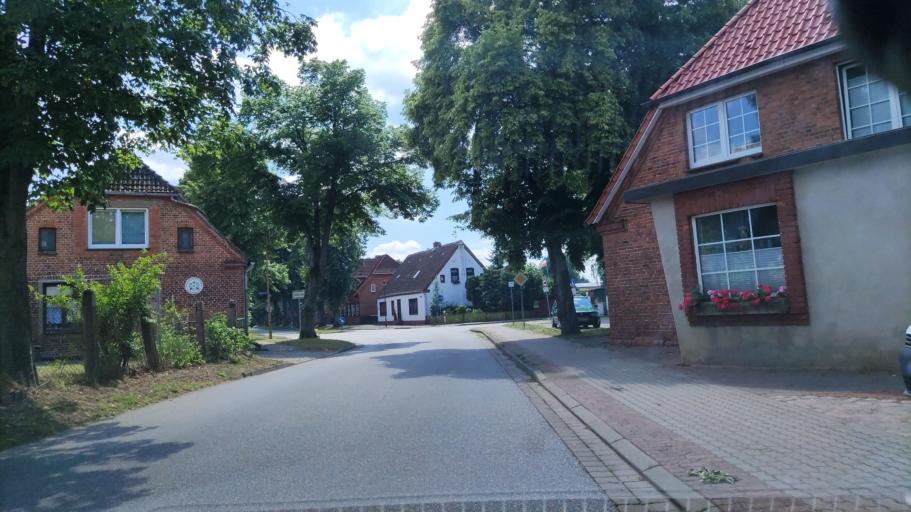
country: DE
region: Mecklenburg-Vorpommern
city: Lubtheen
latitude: 53.3074
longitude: 11.0863
